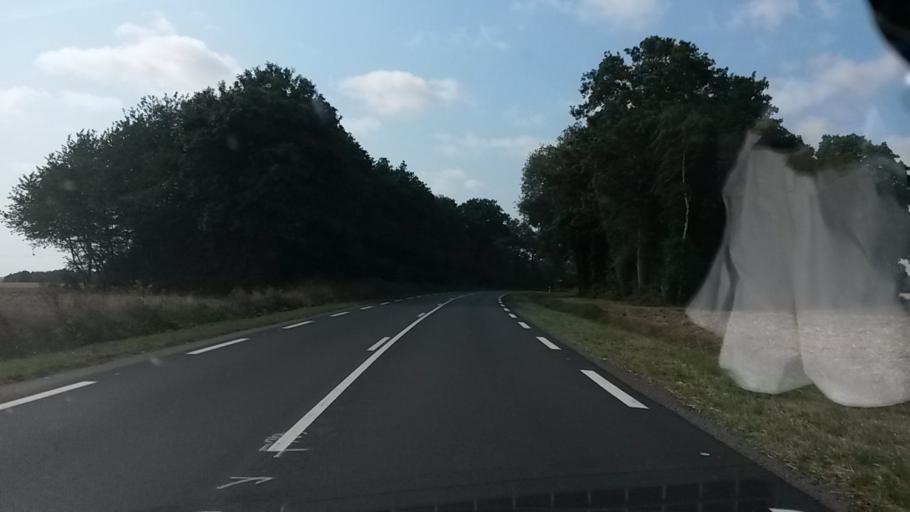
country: FR
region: Haute-Normandie
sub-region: Departement de l'Eure
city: Tillieres-sur-Avre
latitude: 48.7972
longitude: 0.9935
